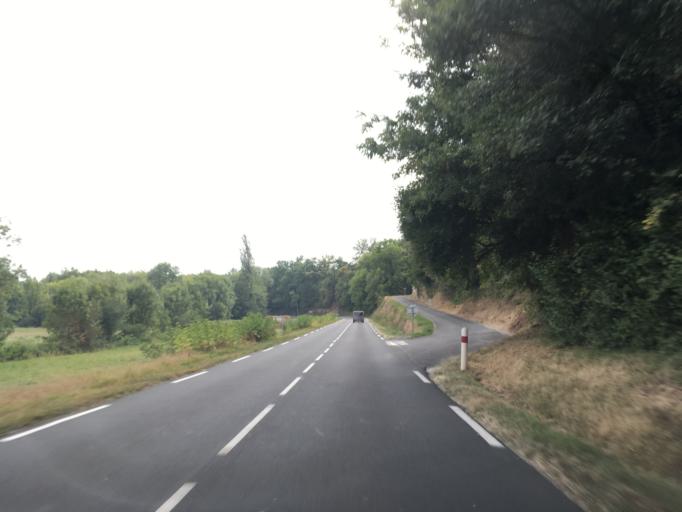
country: FR
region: Aquitaine
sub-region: Departement de la Dordogne
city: Eyvigues-et-Eybenes
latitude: 44.8847
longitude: 1.3801
